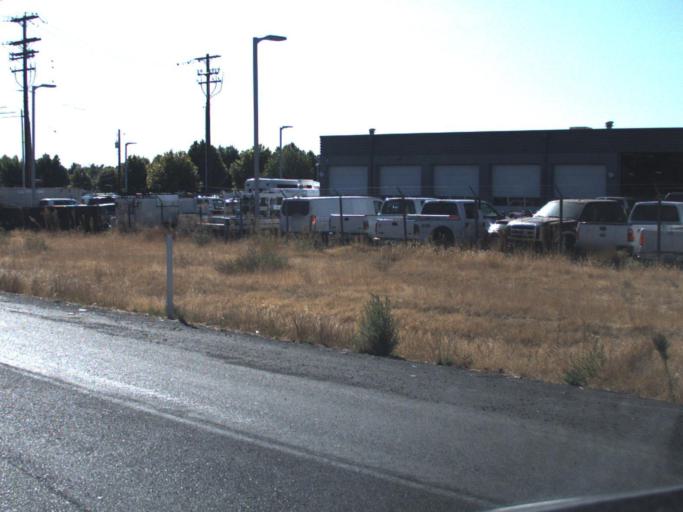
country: US
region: Washington
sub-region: Benton County
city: Kennewick
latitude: 46.2381
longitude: -119.1303
